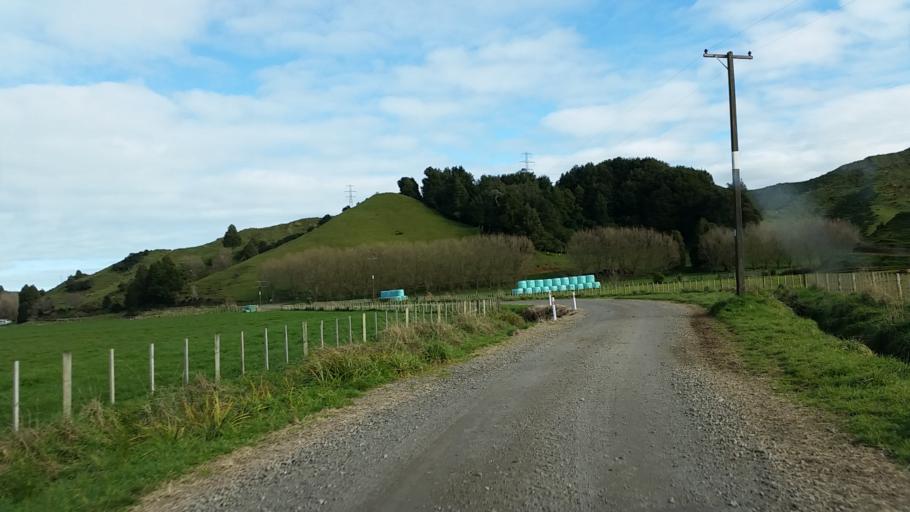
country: NZ
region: Taranaki
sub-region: South Taranaki District
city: Eltham
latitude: -39.2507
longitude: 174.5371
